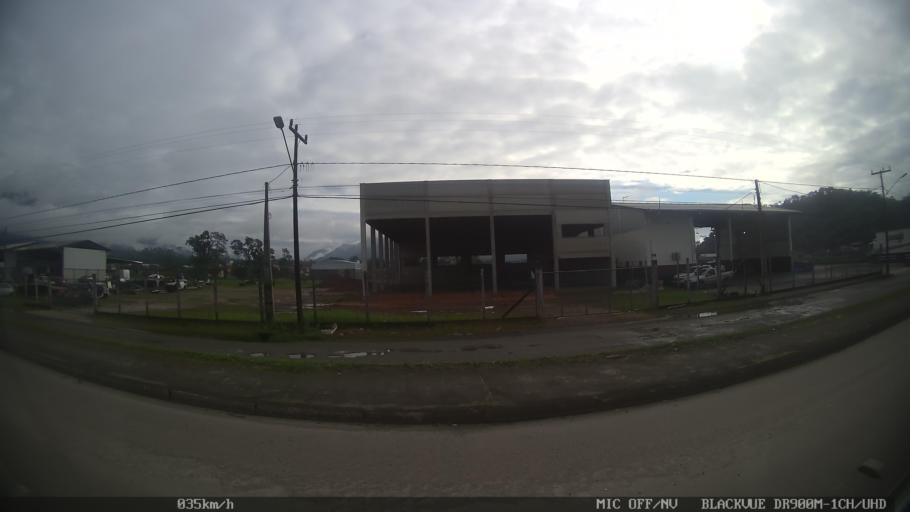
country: BR
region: Santa Catarina
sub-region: Joinville
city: Joinville
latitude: -26.0294
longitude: -48.8510
